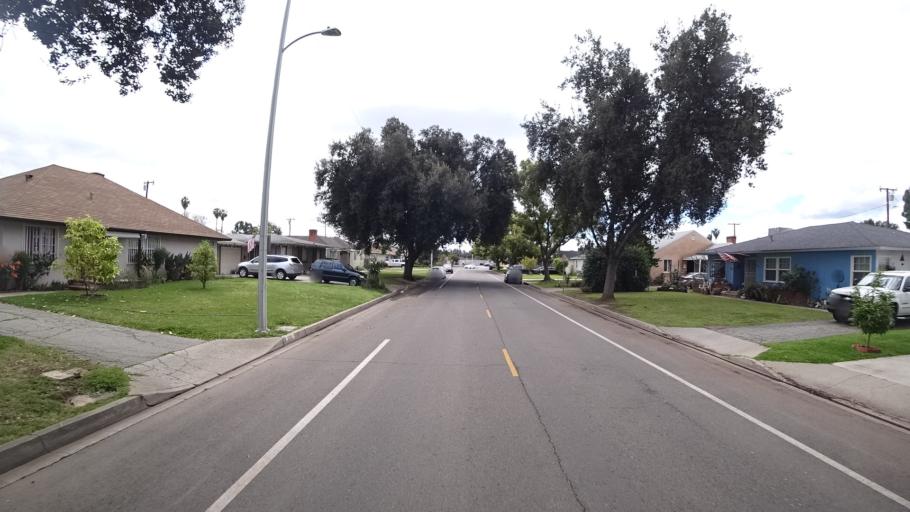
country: US
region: California
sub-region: Los Angeles County
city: West Covina
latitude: 34.0758
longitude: -117.9457
